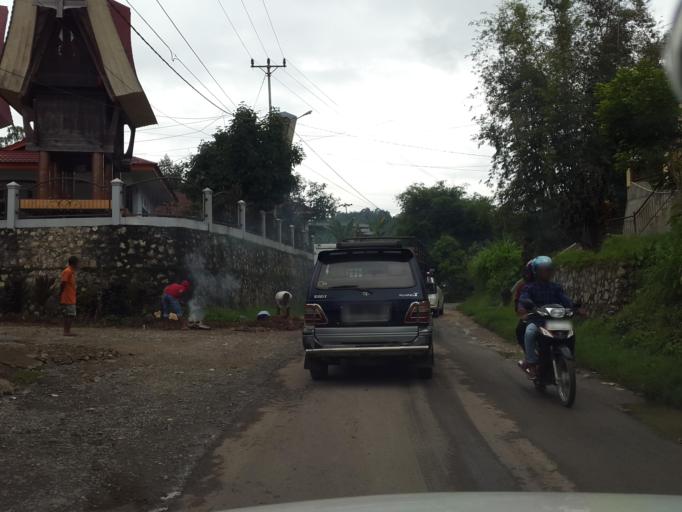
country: ID
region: South Sulawesi
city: Rantepang
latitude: -2.9282
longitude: 119.9415
